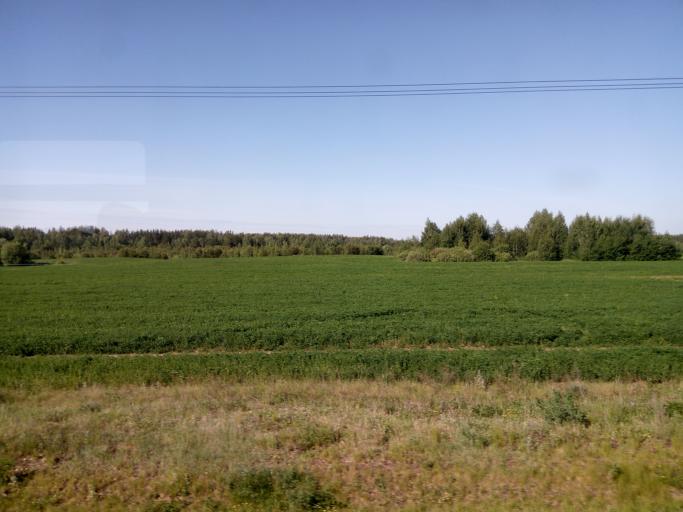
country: RU
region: Tatarstan
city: Stolbishchi
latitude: 55.6871
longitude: 49.1991
